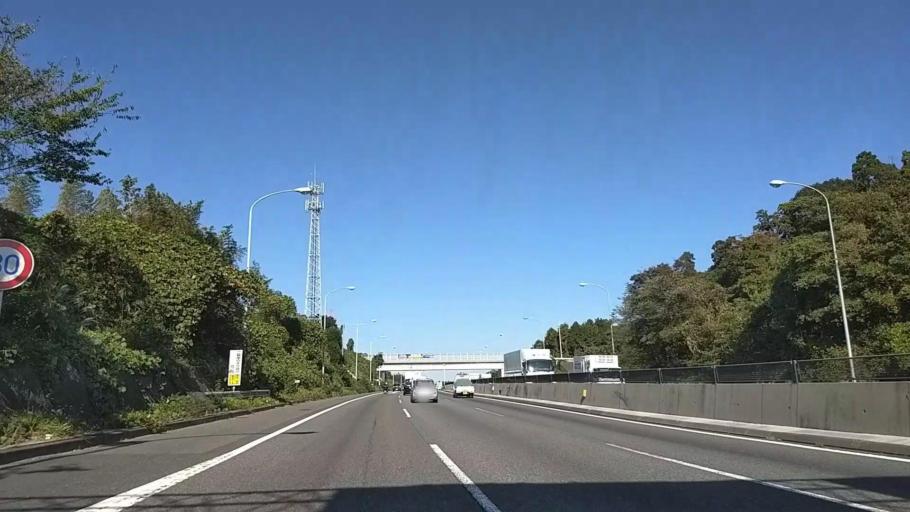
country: JP
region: Kanagawa
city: Minami-rinkan
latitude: 35.4850
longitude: 139.5099
